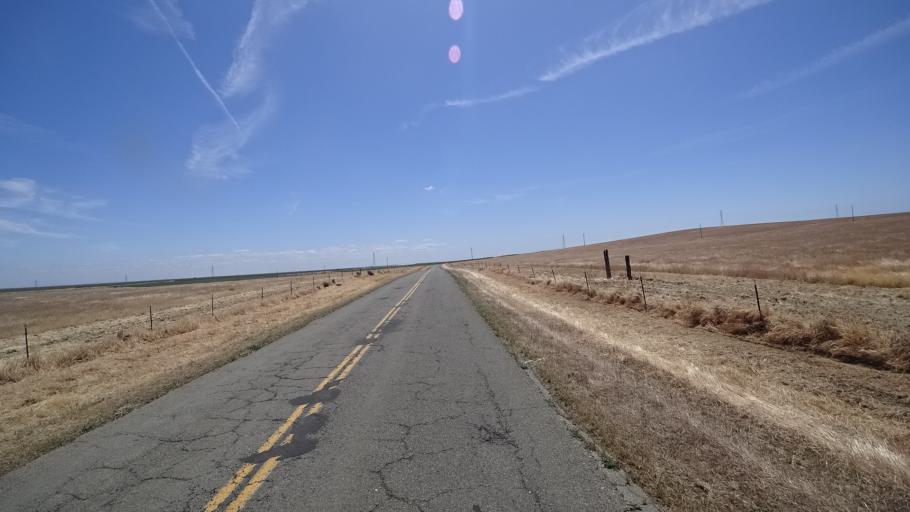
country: US
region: California
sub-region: Kings County
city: Kettleman City
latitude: 35.7926
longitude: -119.8913
